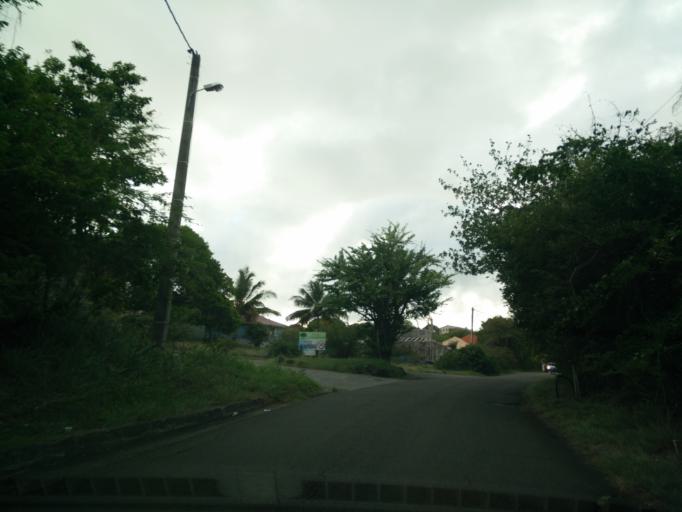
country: MQ
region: Martinique
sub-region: Martinique
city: Le Marin
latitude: 14.4477
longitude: -60.8376
